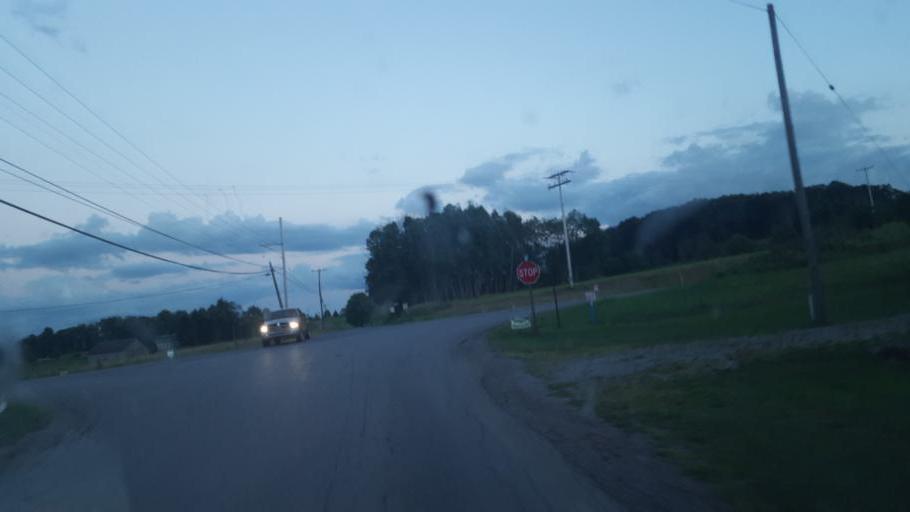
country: US
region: Pennsylvania
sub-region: Clarion County
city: Knox
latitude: 41.2144
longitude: -79.5392
